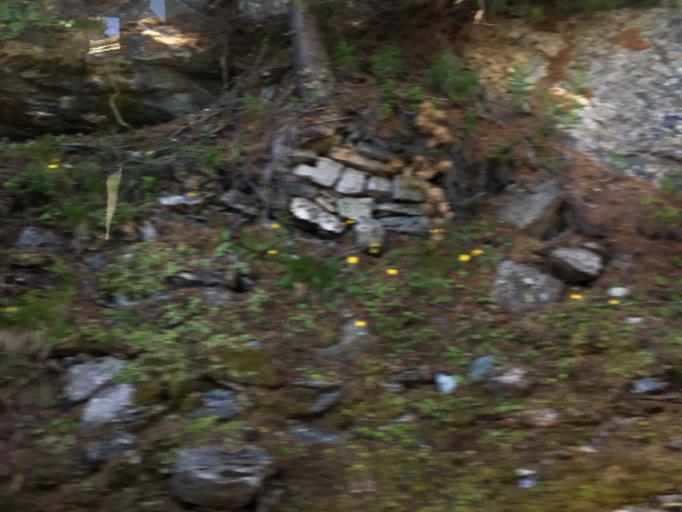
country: CH
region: Valais
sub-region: Visp District
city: Zermatt
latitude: 46.0049
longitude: 7.7528
